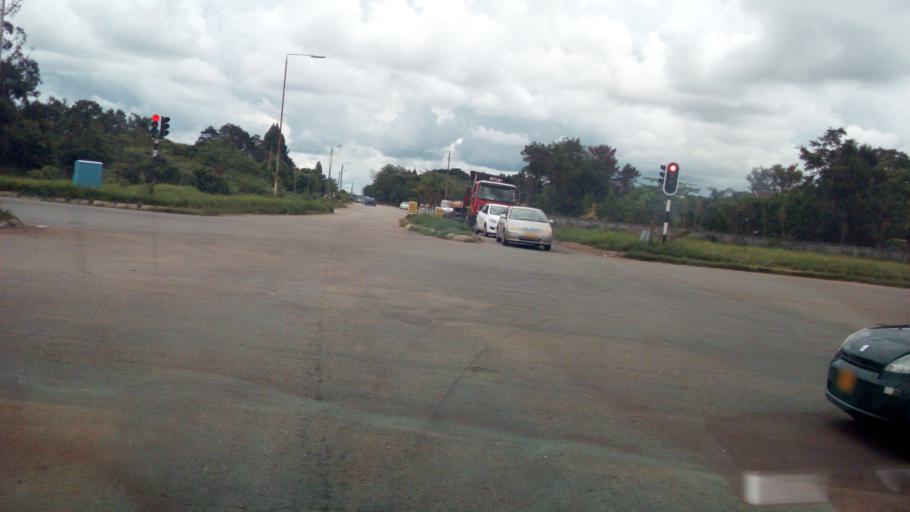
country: ZW
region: Harare
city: Harare
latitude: -17.7654
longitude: 30.9971
